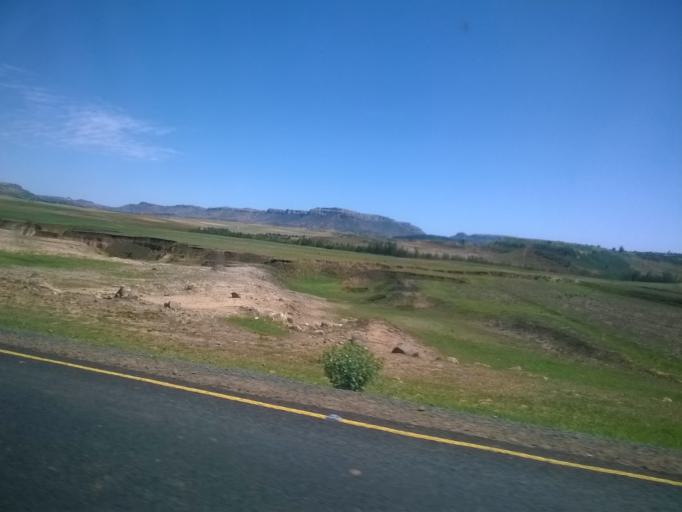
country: LS
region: Berea
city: Teyateyaneng
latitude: -29.0852
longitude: 27.9120
